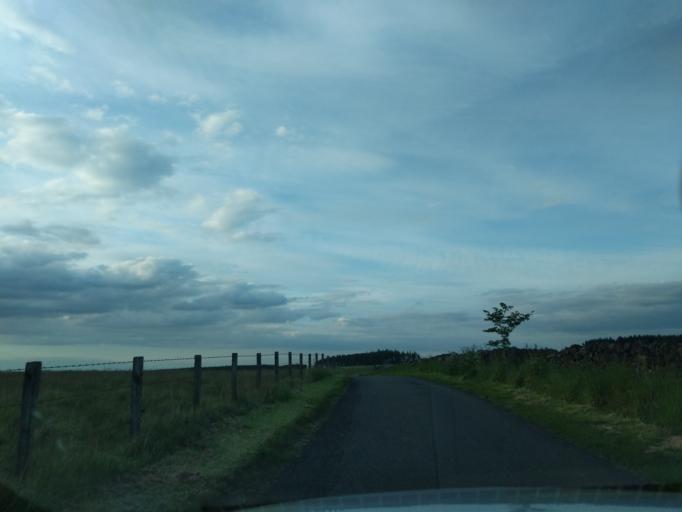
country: GB
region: Scotland
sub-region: Midlothian
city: Gorebridge
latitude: 55.7775
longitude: -3.1025
